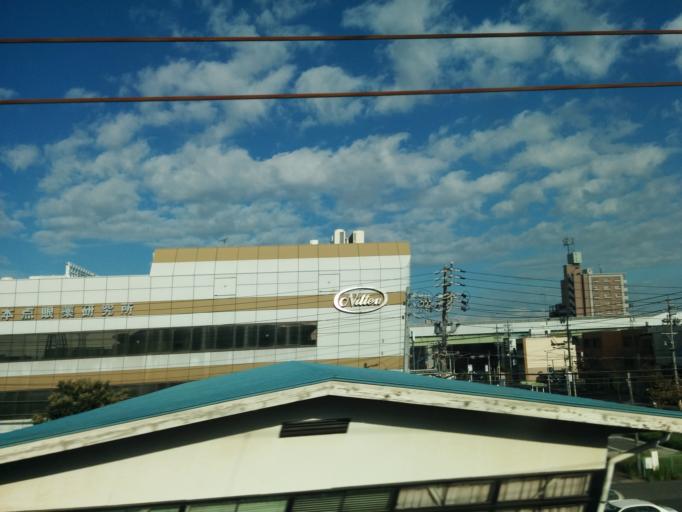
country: JP
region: Aichi
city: Nagoya-shi
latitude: 35.0969
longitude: 136.9259
